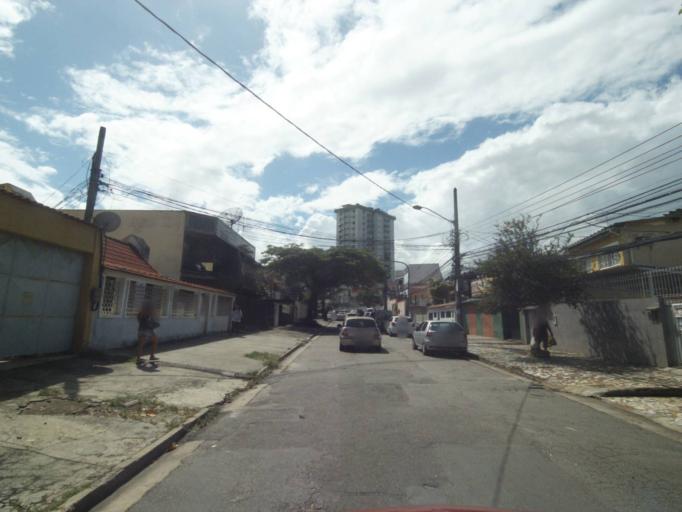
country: BR
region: Rio de Janeiro
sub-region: Sao Joao De Meriti
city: Sao Joao de Meriti
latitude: -22.9261
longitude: -43.3584
